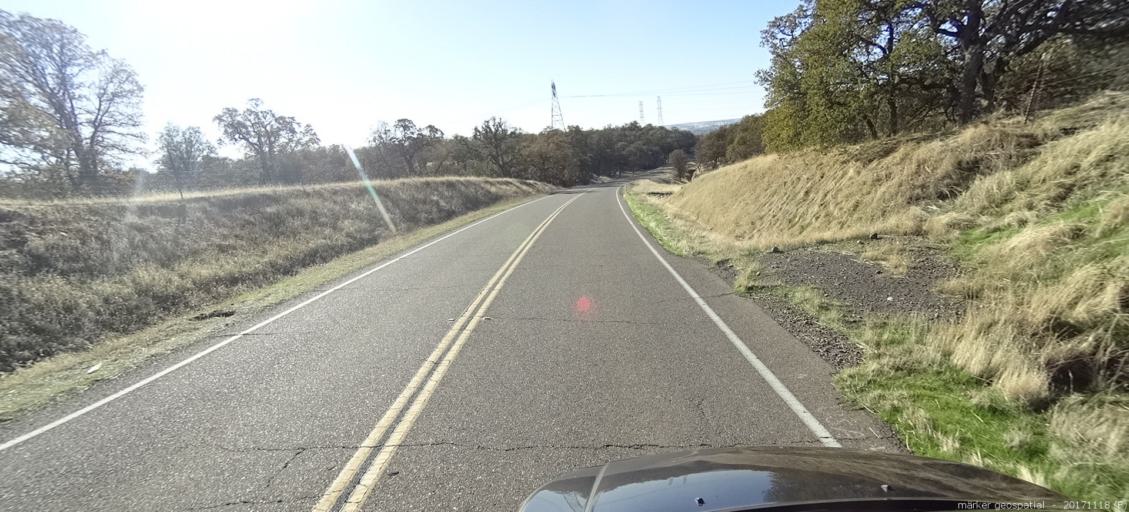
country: US
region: California
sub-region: Shasta County
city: Cottonwood
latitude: 40.4102
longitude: -122.2714
